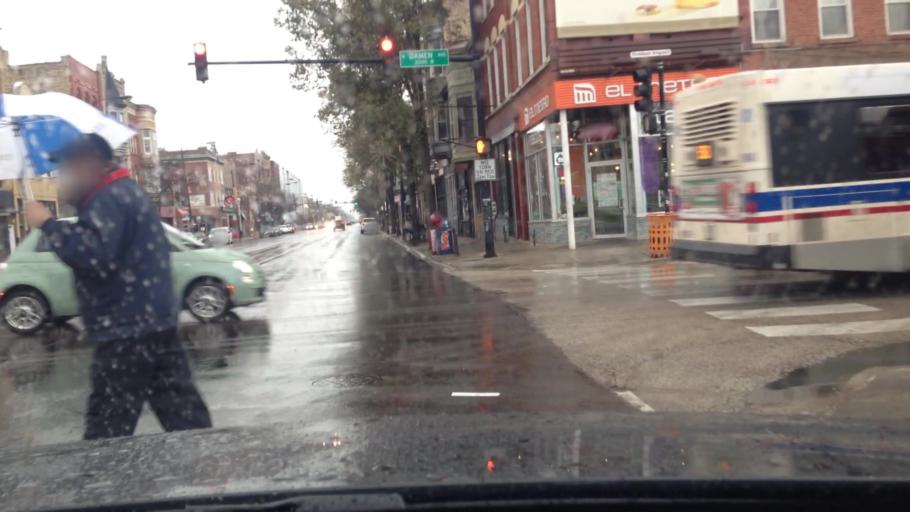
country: US
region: Illinois
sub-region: Cook County
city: Chicago
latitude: 41.8959
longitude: -87.6772
